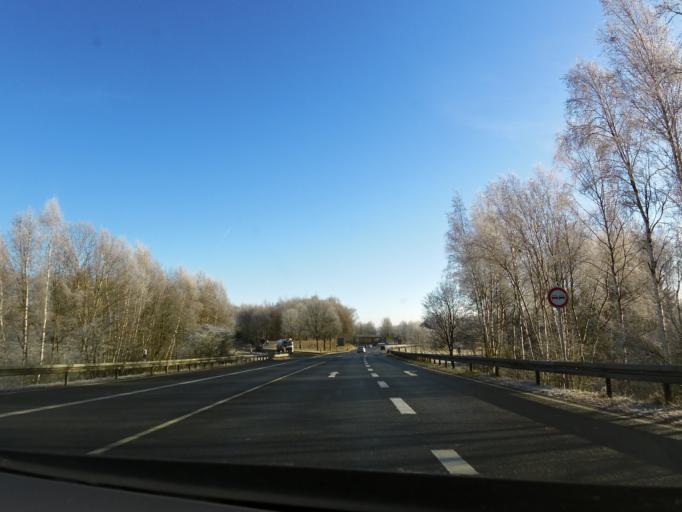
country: DE
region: Bavaria
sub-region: Upper Franconia
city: Marktredwitz
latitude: 50.0118
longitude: 12.0720
